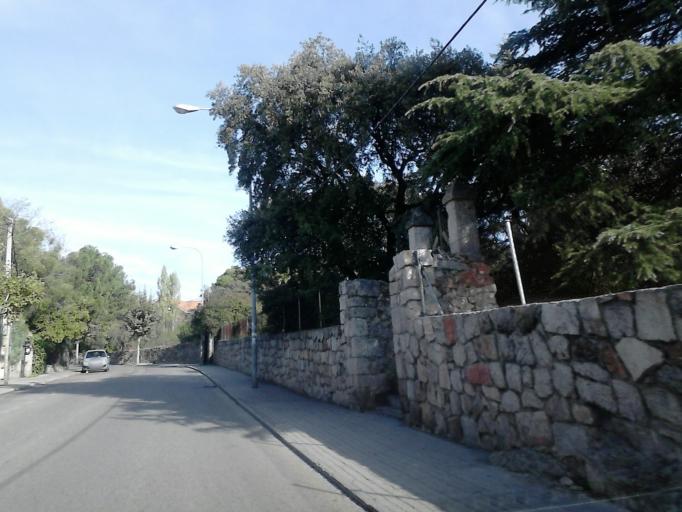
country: ES
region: Madrid
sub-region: Provincia de Madrid
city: Torrelodones
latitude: 40.5756
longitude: -3.9570
